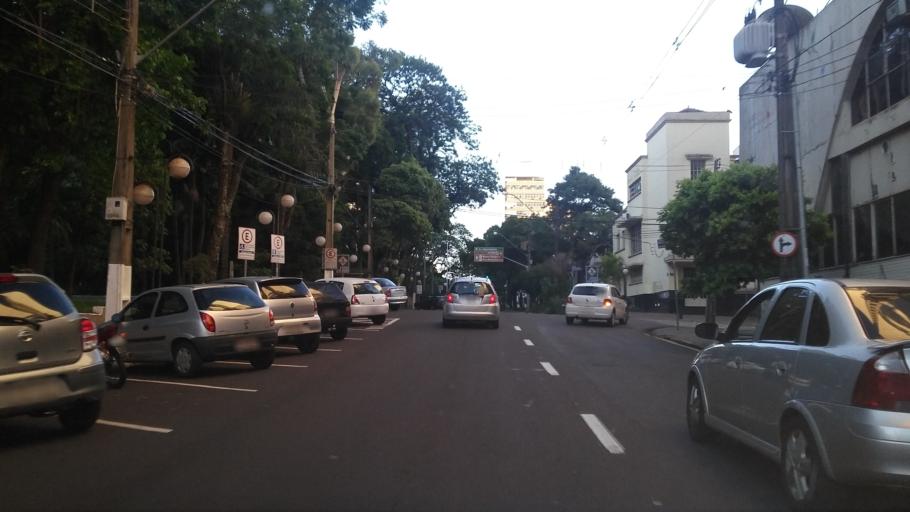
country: BR
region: Parana
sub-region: Londrina
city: Londrina
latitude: -23.3137
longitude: -51.1589
